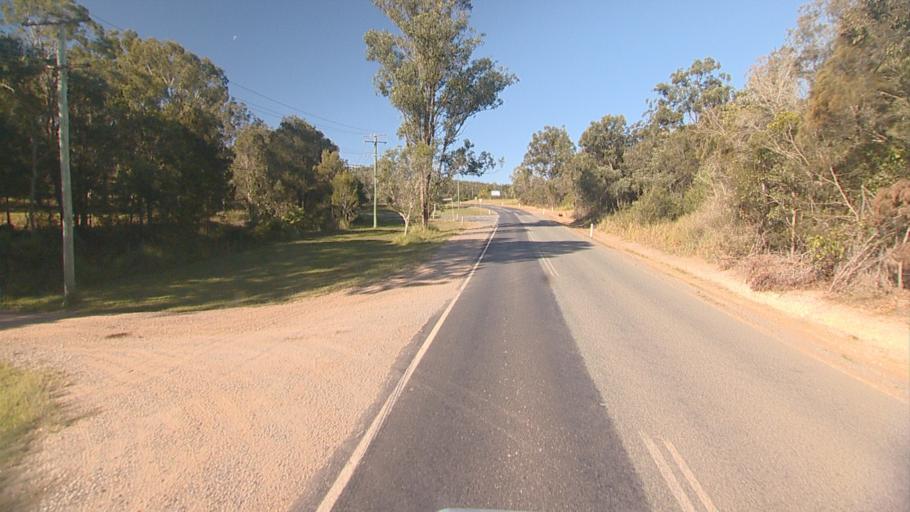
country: AU
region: Queensland
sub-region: Logan
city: Logan Reserve
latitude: -27.7460
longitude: 153.1371
